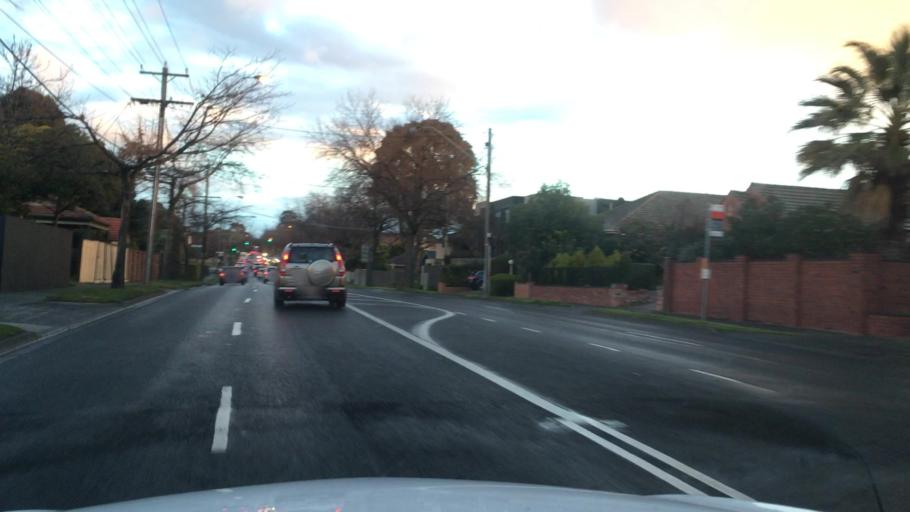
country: AU
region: Victoria
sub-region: Whitehorse
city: Box Hill
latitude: -37.8199
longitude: 145.1145
